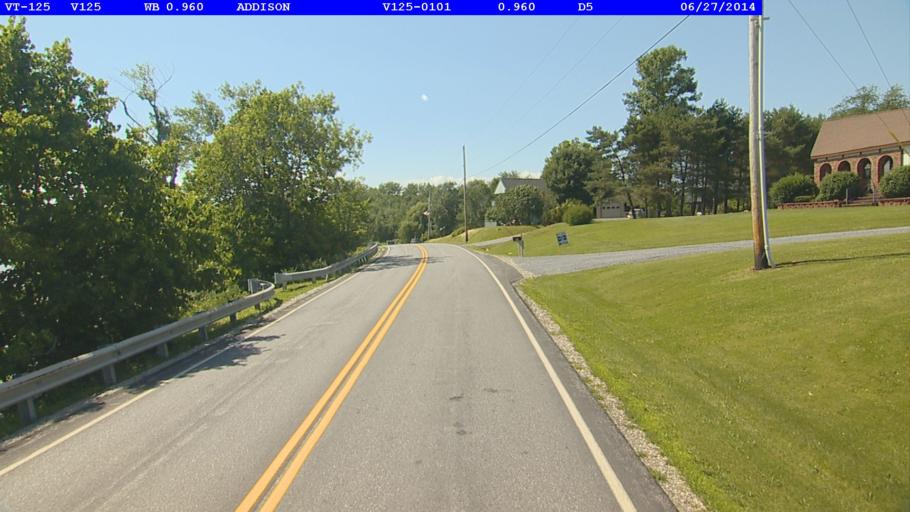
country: US
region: New York
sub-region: Essex County
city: Port Henry
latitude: 44.0295
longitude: -73.4022
